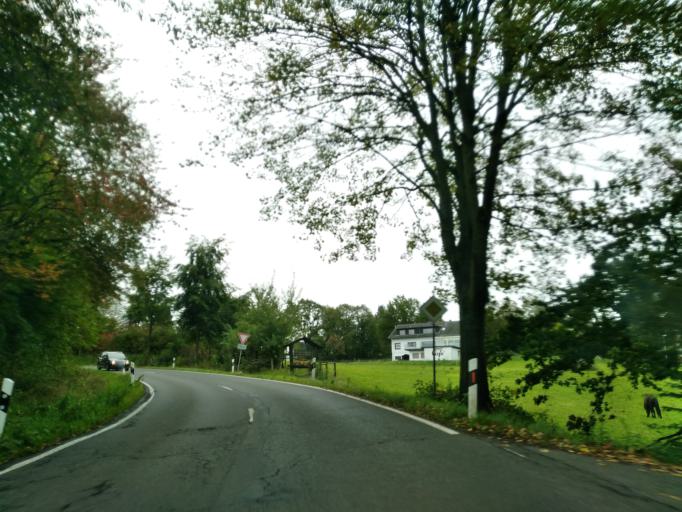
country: DE
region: Rheinland-Pfalz
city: Windhagen
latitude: 50.6636
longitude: 7.2986
